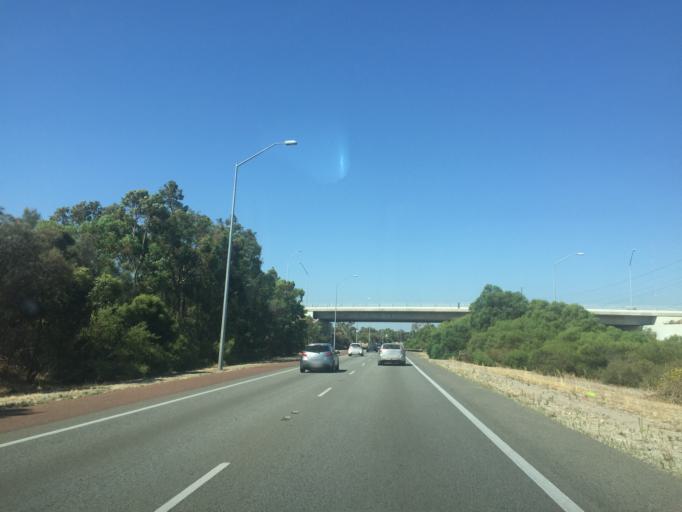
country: AU
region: Western Australia
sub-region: Canning
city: Canning Vale
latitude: -32.0579
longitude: 115.9037
